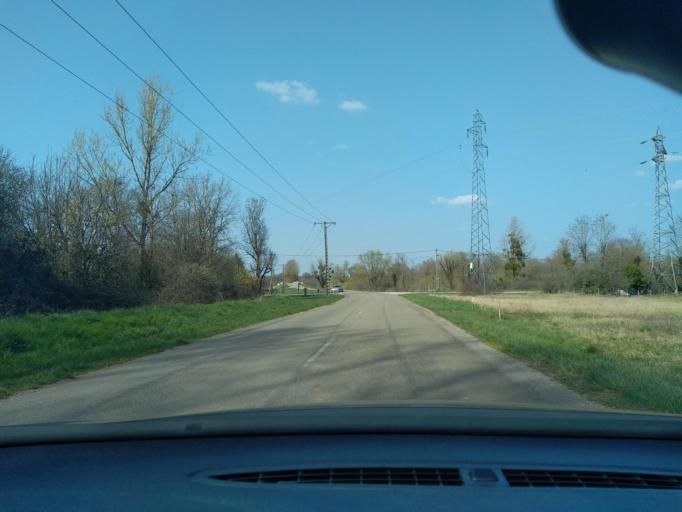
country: FR
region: Franche-Comte
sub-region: Departement du Jura
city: Mont-sous-Vaudrey
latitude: 47.0068
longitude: 5.5964
